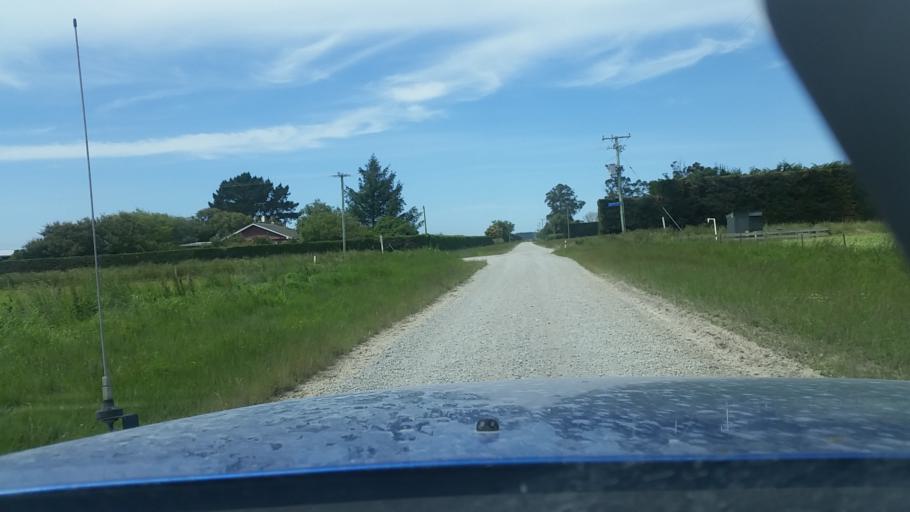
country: NZ
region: Canterbury
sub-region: Ashburton District
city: Tinwald
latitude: -44.0640
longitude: 171.7536
